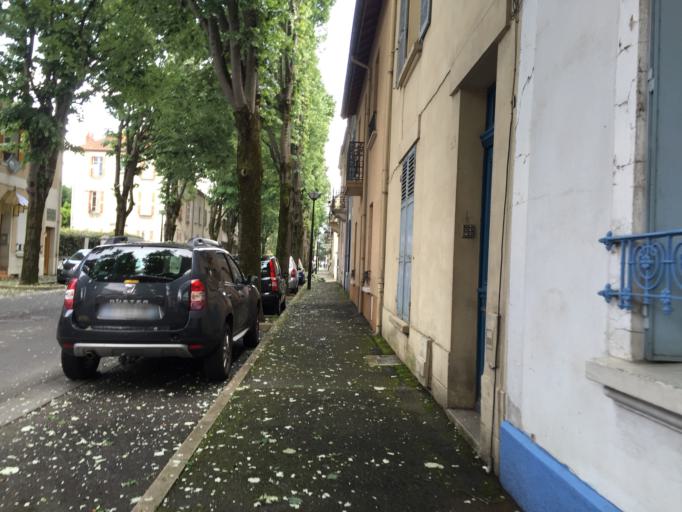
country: FR
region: Auvergne
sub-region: Departement de l'Allier
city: Vichy
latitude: 46.1258
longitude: 3.4347
